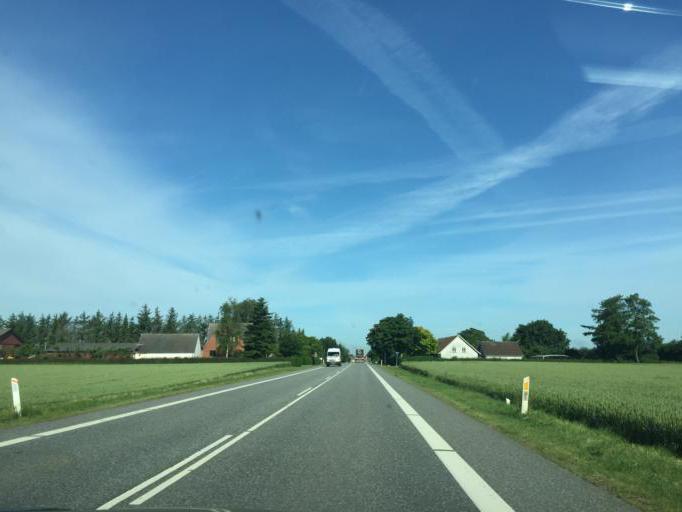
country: DK
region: South Denmark
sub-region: Middelfart Kommune
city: Norre Aby
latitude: 55.4663
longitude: 9.9094
